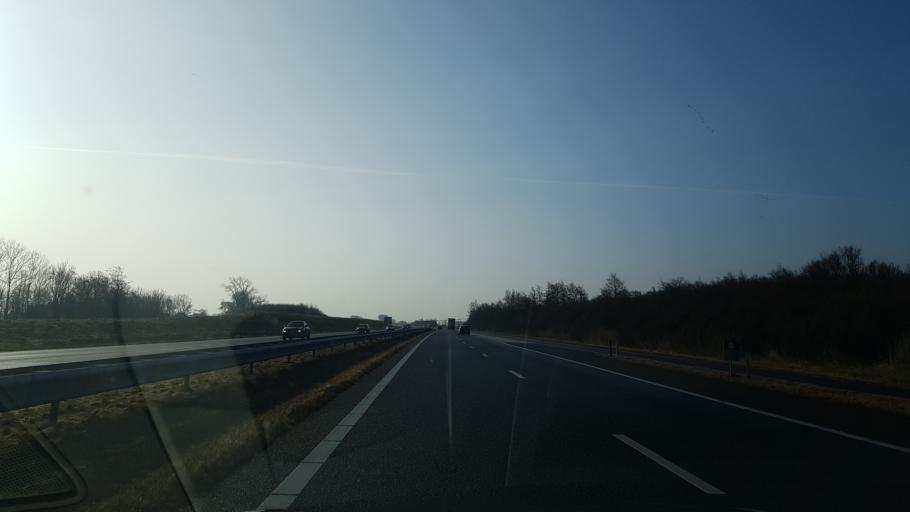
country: NL
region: Friesland
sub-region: Gemeente Boarnsterhim
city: Grou
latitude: 53.1082
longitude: 5.8148
